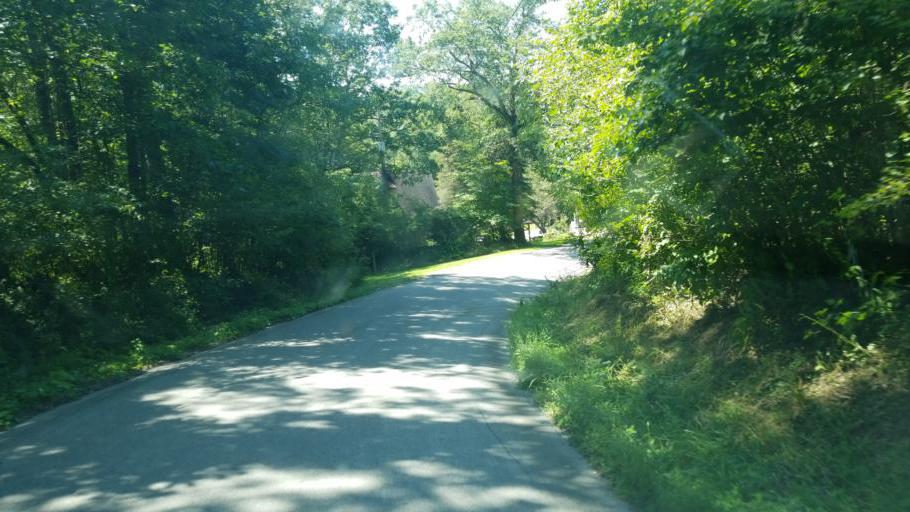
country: US
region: Pennsylvania
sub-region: Clarion County
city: Knox
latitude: 41.1949
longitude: -79.6120
